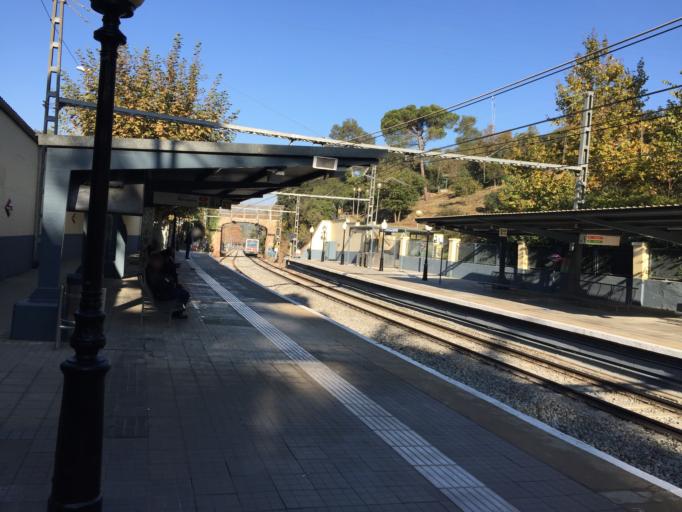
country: ES
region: Catalonia
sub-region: Provincia de Barcelona
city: Sant Just Desvern
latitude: 41.4200
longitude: 2.0970
